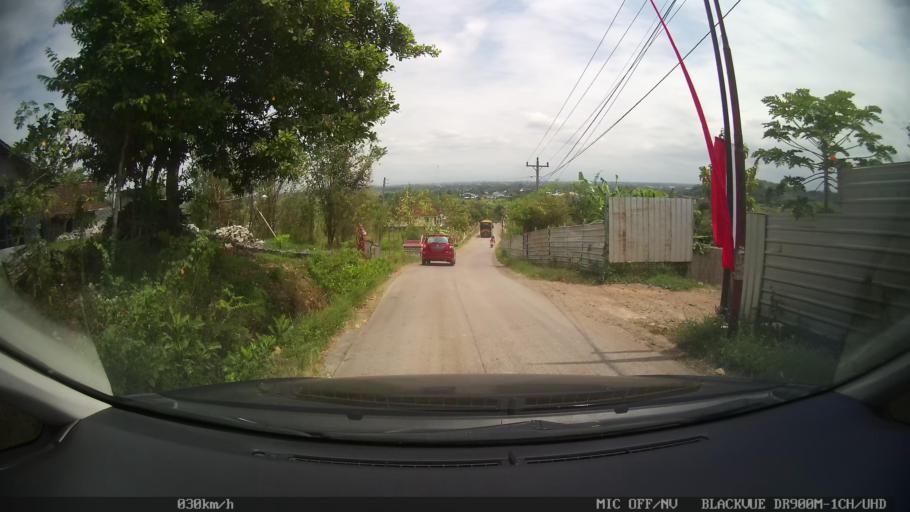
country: ID
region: Central Java
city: Candi Prambanan
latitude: -7.7839
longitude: 110.4959
